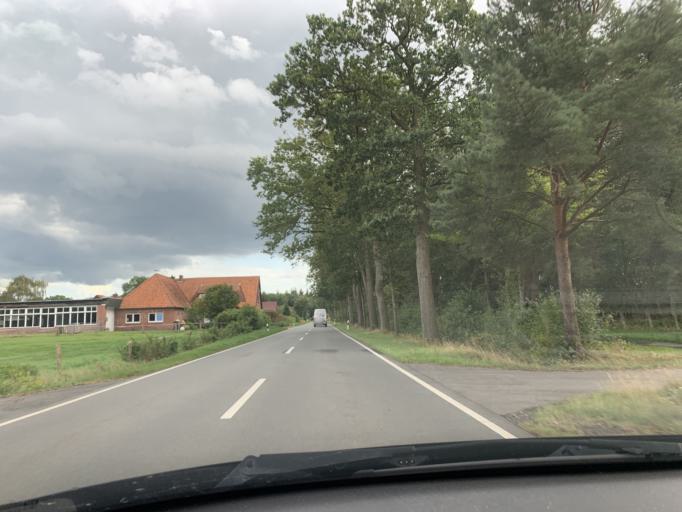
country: DE
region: Lower Saxony
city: Westerstede
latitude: 53.2939
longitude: 7.9205
